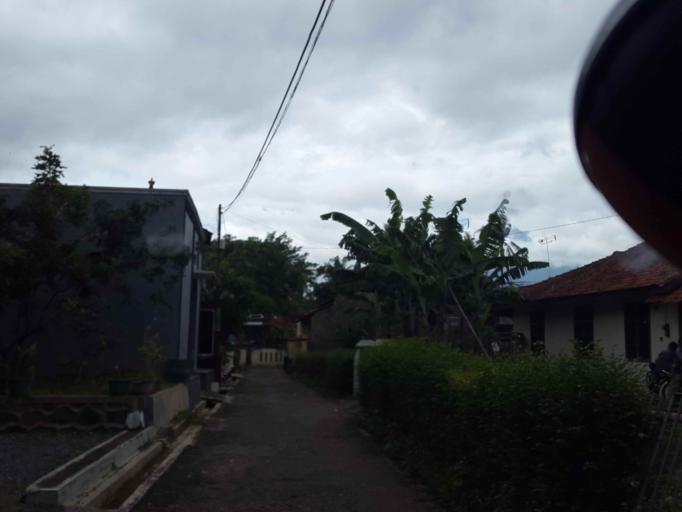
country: ID
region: Central Java
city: Salatiga
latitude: -7.3246
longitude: 110.5126
